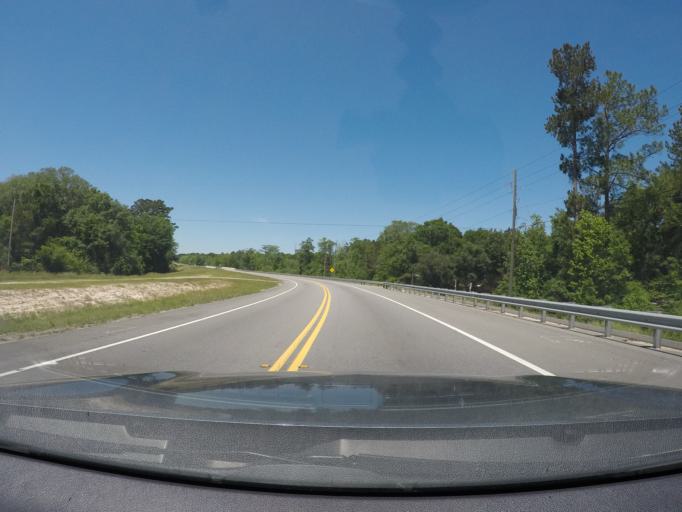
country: US
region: Georgia
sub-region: Chatham County
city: Bloomingdale
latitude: 32.1909
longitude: -81.4062
